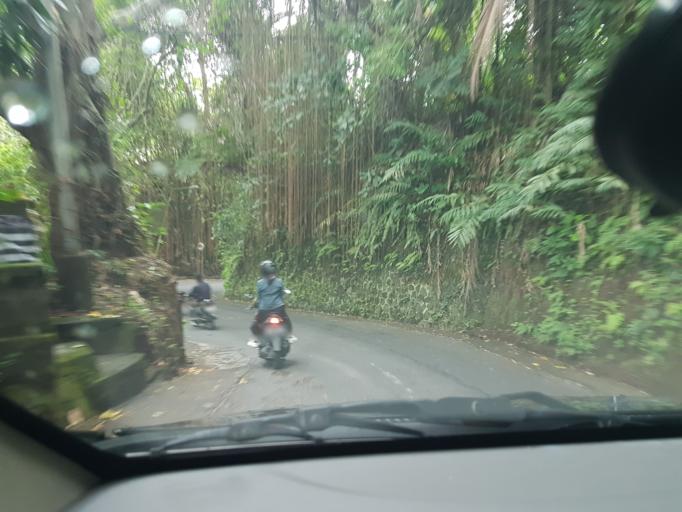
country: ID
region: Bali
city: Banjar Pande
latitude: -8.5061
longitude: 115.2499
